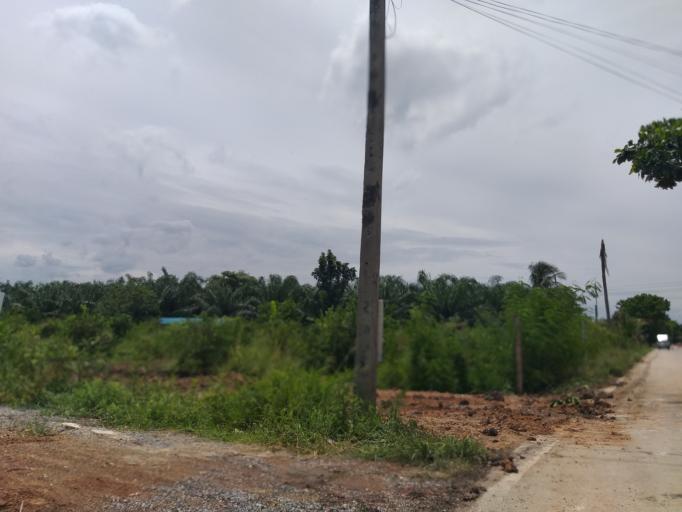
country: TH
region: Pathum Thani
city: Ban Lam Luk Ka
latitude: 14.0335
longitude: 100.8662
